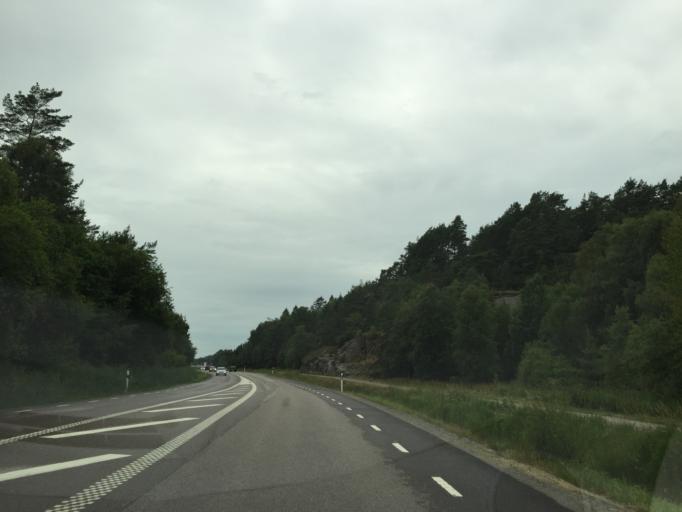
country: SE
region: Vaestra Goetaland
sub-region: Tjorns Kommun
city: Myggenas
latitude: 58.0246
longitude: 11.6747
